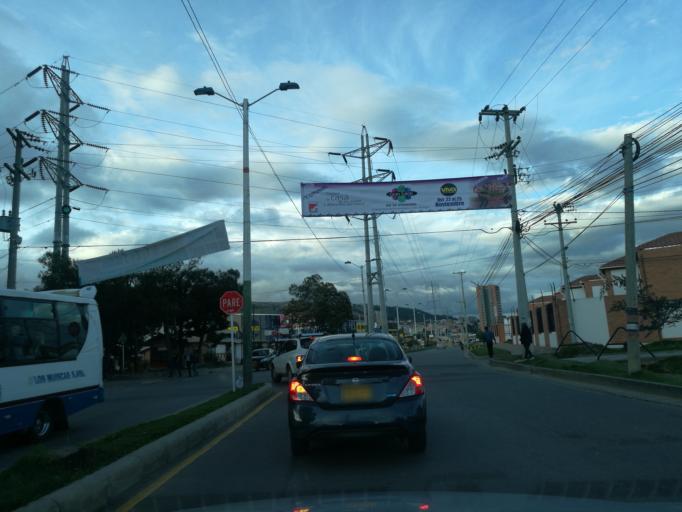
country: CO
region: Boyaca
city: Tunja
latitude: 5.5545
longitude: -73.3456
